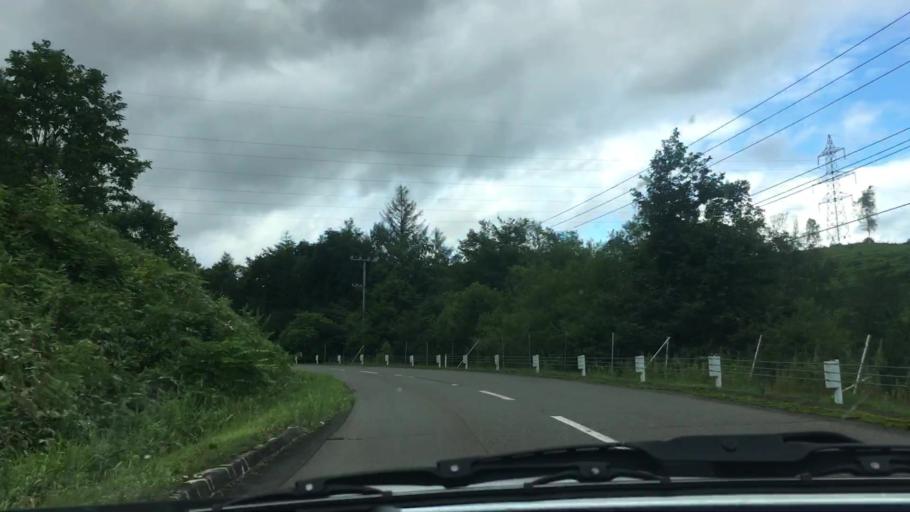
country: JP
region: Hokkaido
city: Otofuke
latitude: 43.1565
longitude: 142.8546
